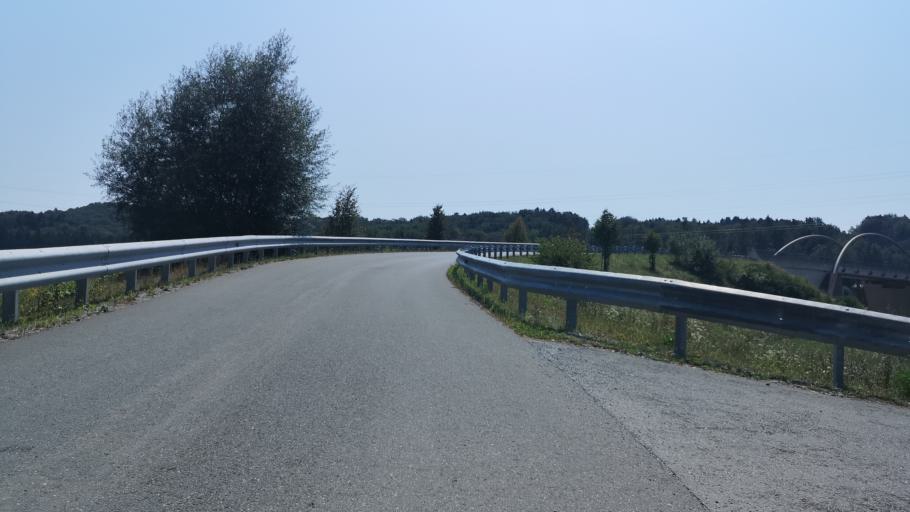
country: AT
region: Styria
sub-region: Politischer Bezirk Deutschlandsberg
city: Gross Sankt Florian
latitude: 46.8161
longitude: 15.2879
